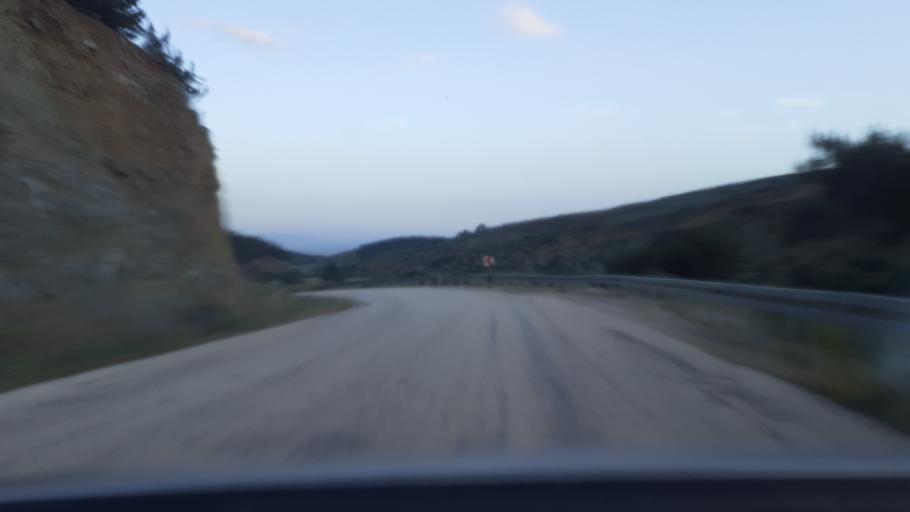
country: TR
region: Hatay
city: Kirikhan
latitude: 36.5165
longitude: 36.3186
